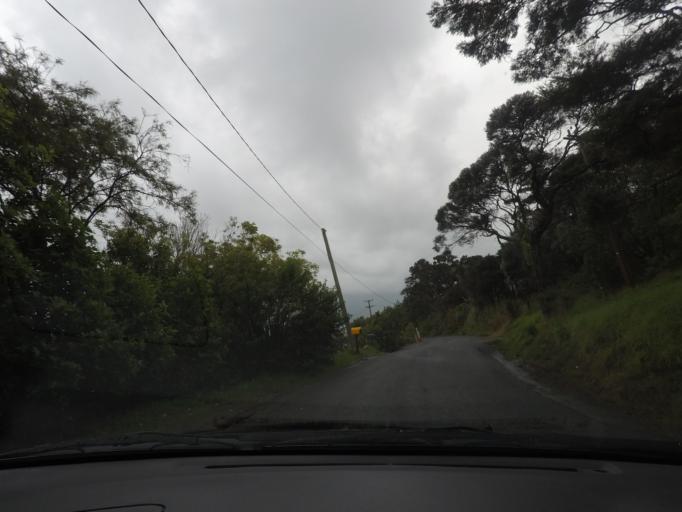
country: NZ
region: Auckland
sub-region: Auckland
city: Warkworth
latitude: -36.4829
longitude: 174.7279
